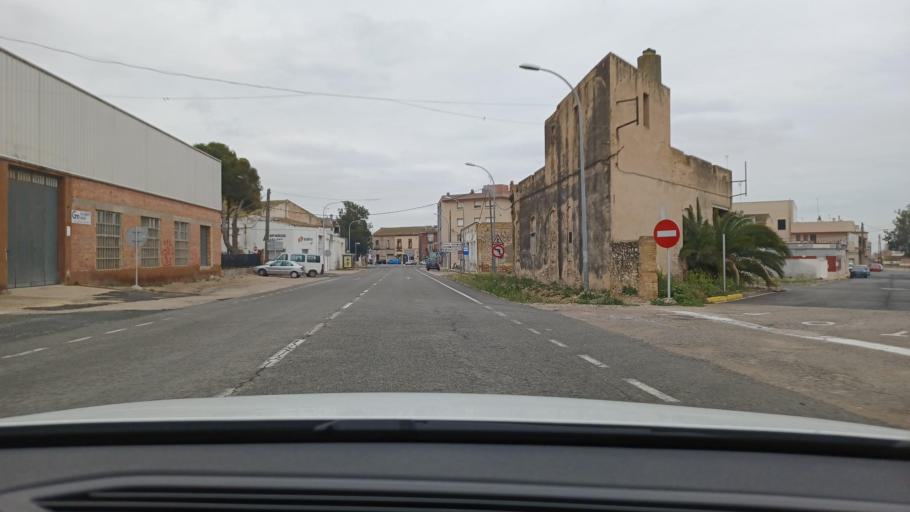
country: ES
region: Catalonia
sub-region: Provincia de Tarragona
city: Camarles
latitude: 40.7487
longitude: 0.6213
